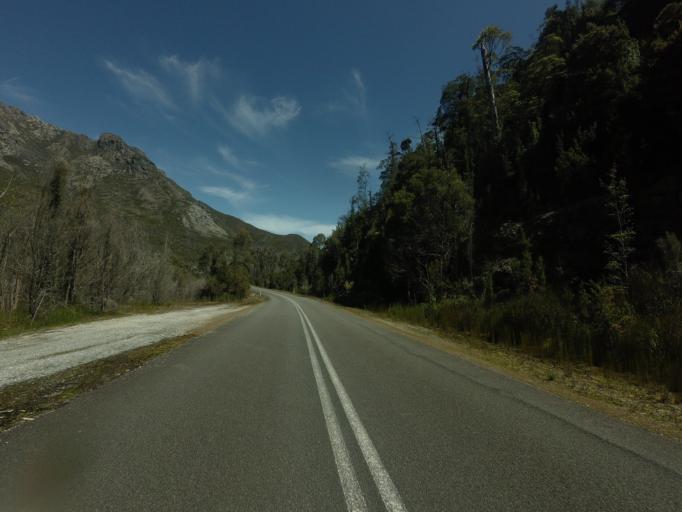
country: AU
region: Tasmania
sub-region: Huon Valley
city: Geeveston
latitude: -42.8578
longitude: 146.2310
